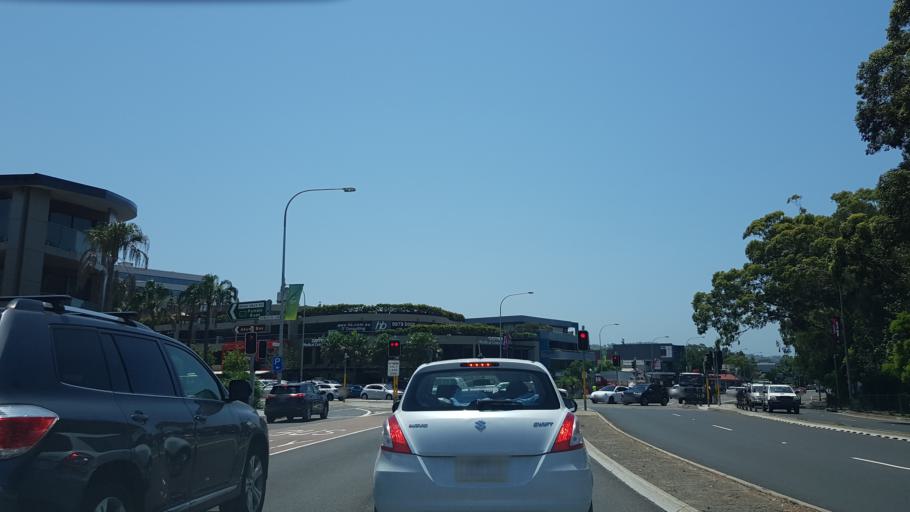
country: AU
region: New South Wales
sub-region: Pittwater
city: Warriewood
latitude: -33.6798
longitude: 151.3027
